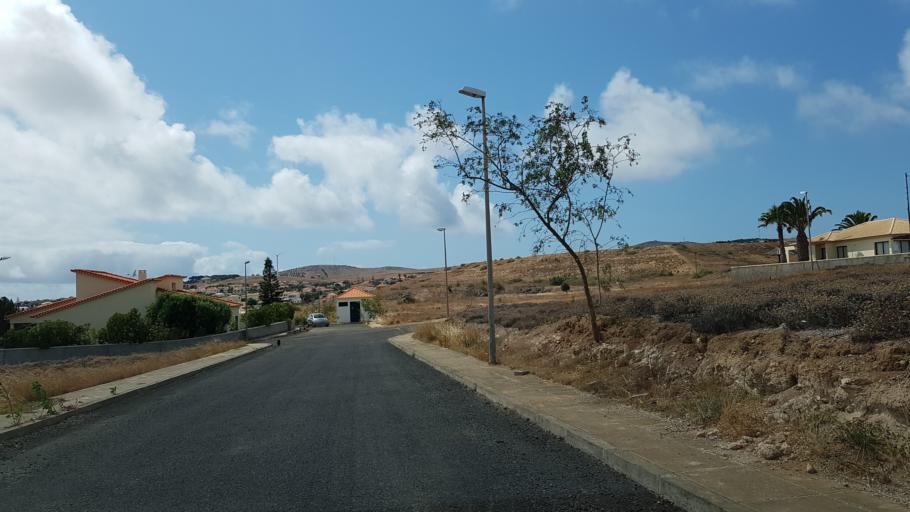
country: PT
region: Madeira
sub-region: Porto Santo
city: Vila de Porto Santo
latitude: 33.0544
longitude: -16.3461
